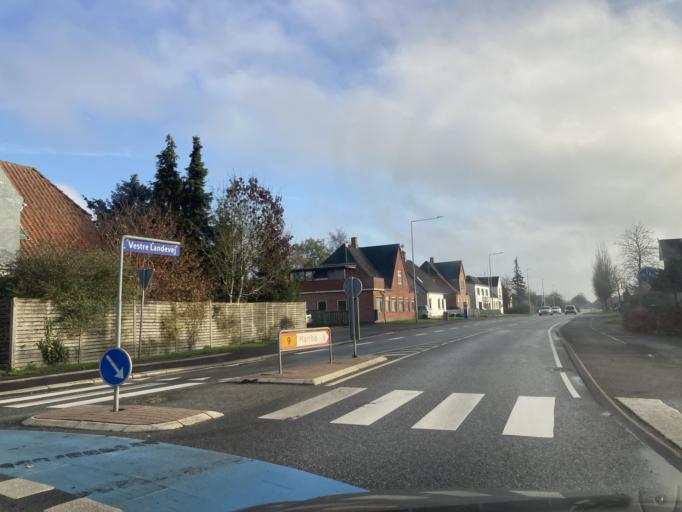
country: DK
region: Zealand
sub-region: Lolland Kommune
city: Maribo
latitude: 54.8065
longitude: 11.4302
